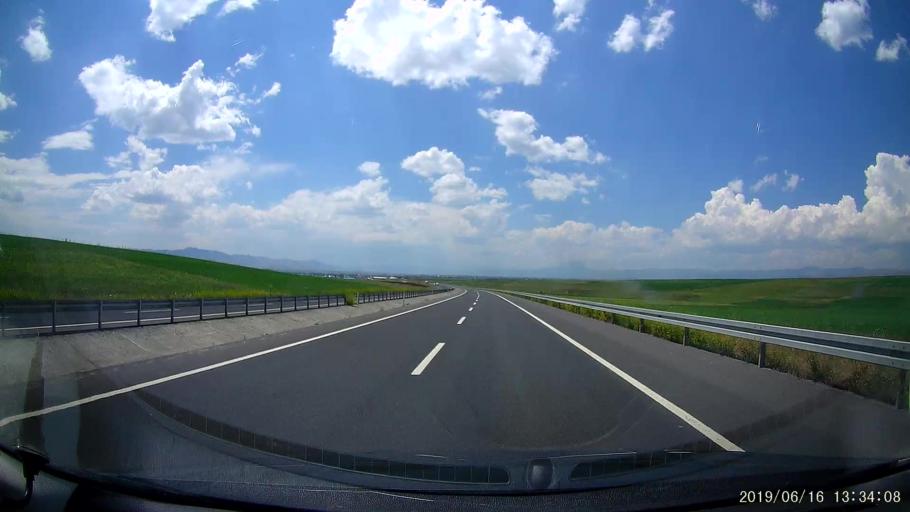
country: TR
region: Agri
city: Agri
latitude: 39.7113
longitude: 43.1351
